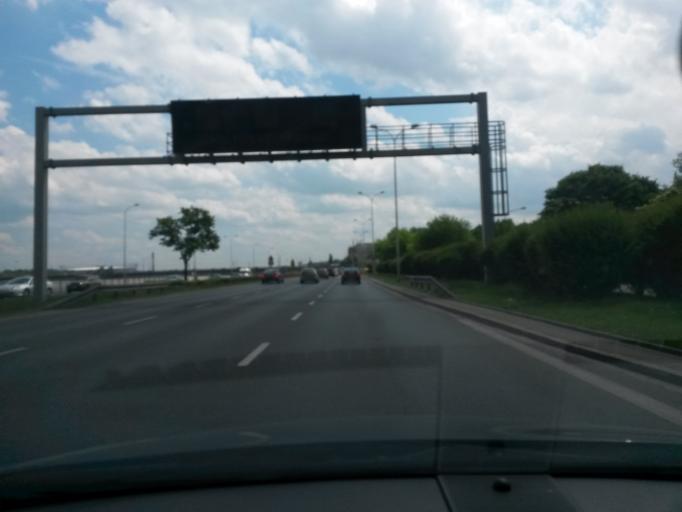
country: PL
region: Masovian Voivodeship
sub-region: Warszawa
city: Praga Polnoc
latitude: 52.2517
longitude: 21.0149
